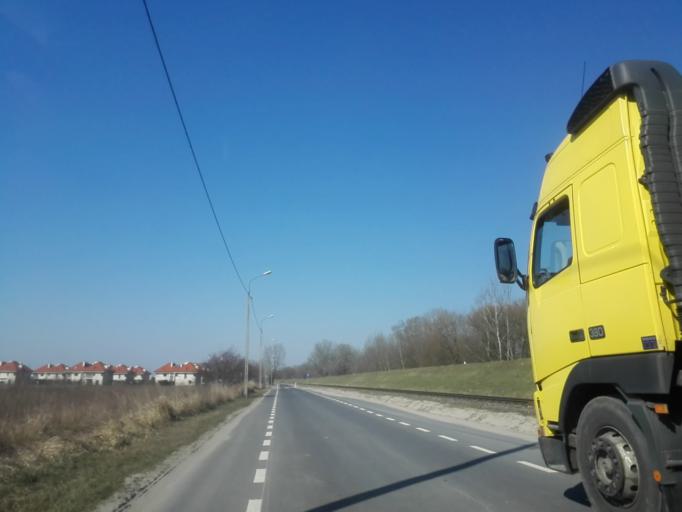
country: PL
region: Masovian Voivodeship
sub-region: Warszawa
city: Wilanow
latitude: 52.1612
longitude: 21.1342
